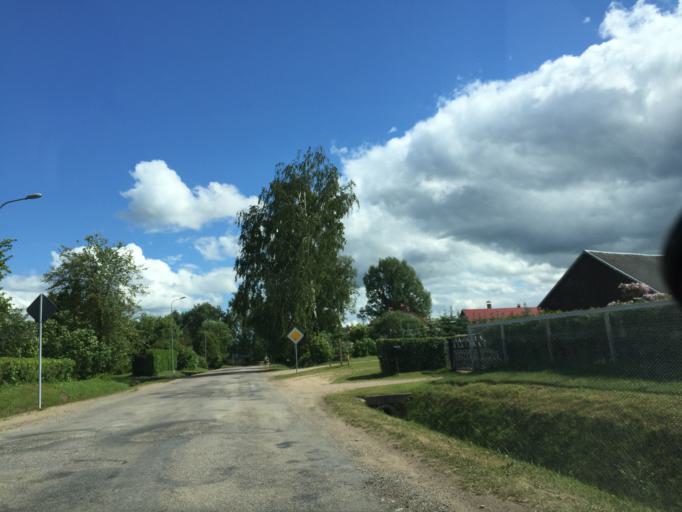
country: LT
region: Panevezys
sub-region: Birzai
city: Birzai
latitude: 56.3829
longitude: 24.6440
